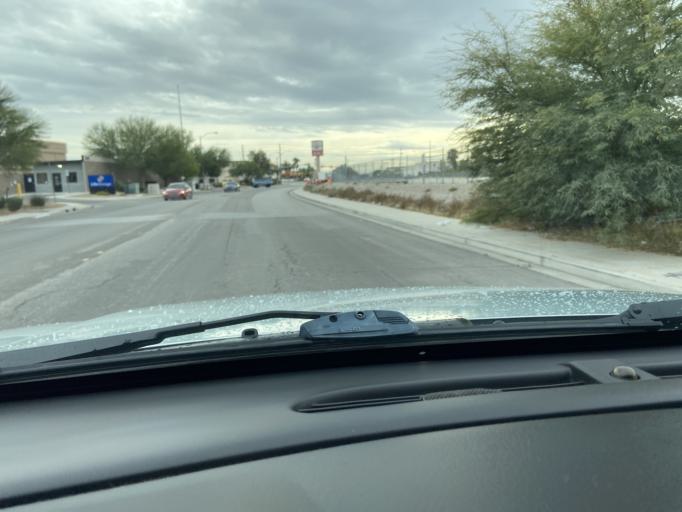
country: US
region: Nevada
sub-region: Clark County
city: North Las Vegas
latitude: 36.2420
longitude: -115.1122
